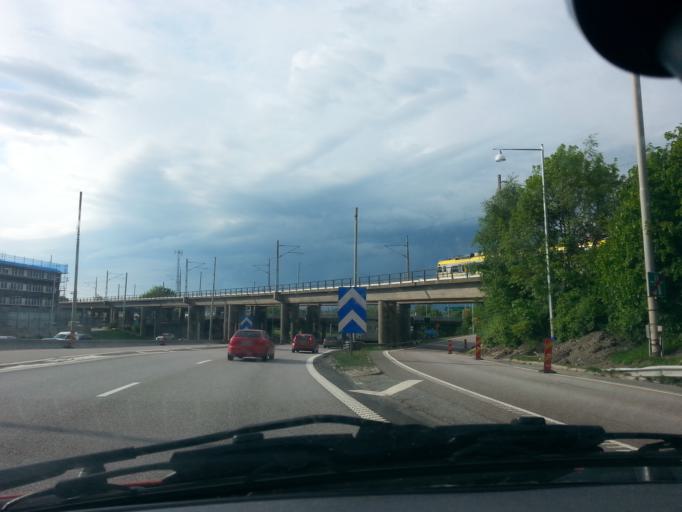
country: SE
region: Vaestra Goetaland
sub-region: Goteborg
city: Goeteborg
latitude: 57.7128
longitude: 11.9953
